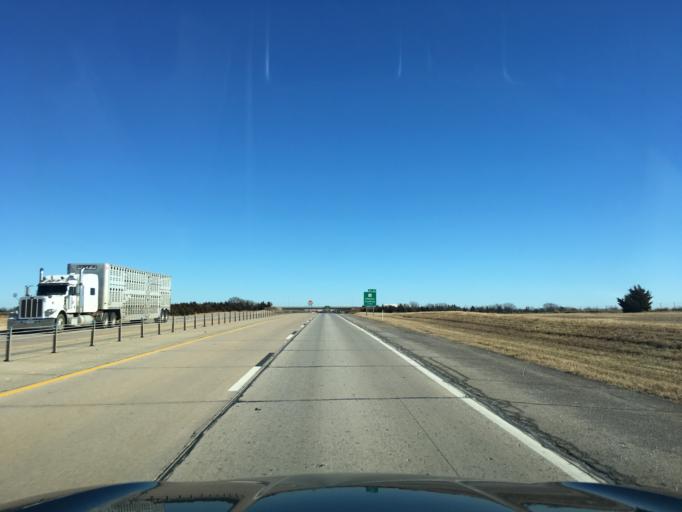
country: US
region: Oklahoma
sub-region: Pawnee County
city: Pawnee
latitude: 36.2247
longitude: -96.8082
